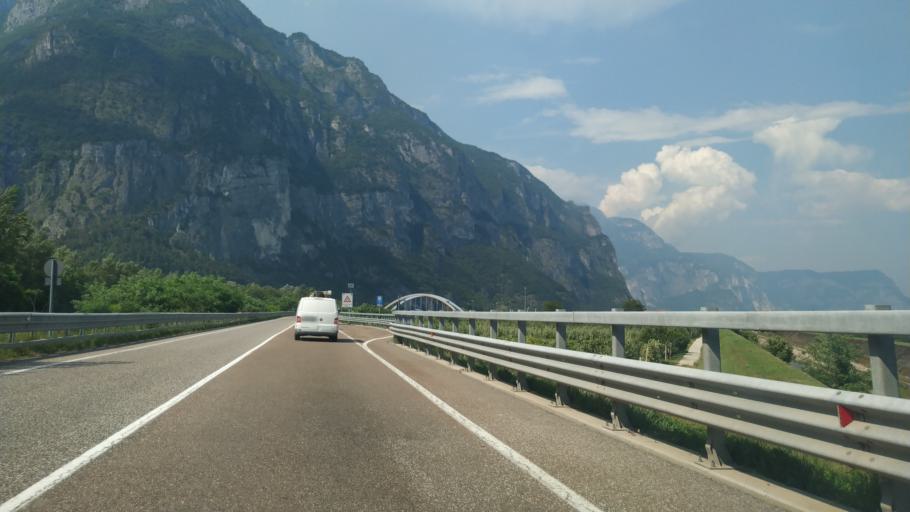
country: IT
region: Trentino-Alto Adige
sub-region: Provincia di Trento
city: Zambana
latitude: 46.1522
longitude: 11.0768
